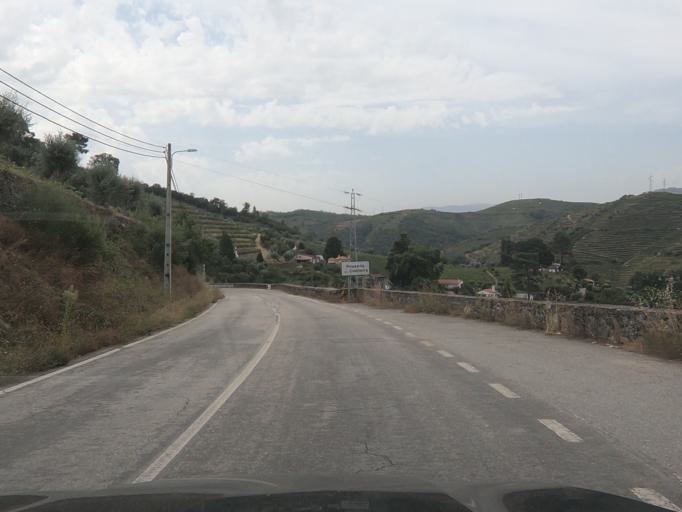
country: PT
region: Vila Real
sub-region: Santa Marta de Penaguiao
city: Santa Marta de Penaguiao
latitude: 41.2303
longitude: -7.7665
